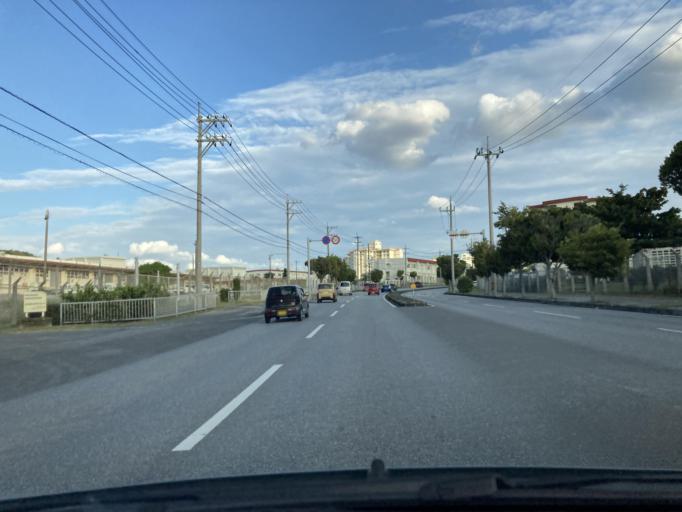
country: JP
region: Okinawa
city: Chatan
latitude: 26.3077
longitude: 127.7684
